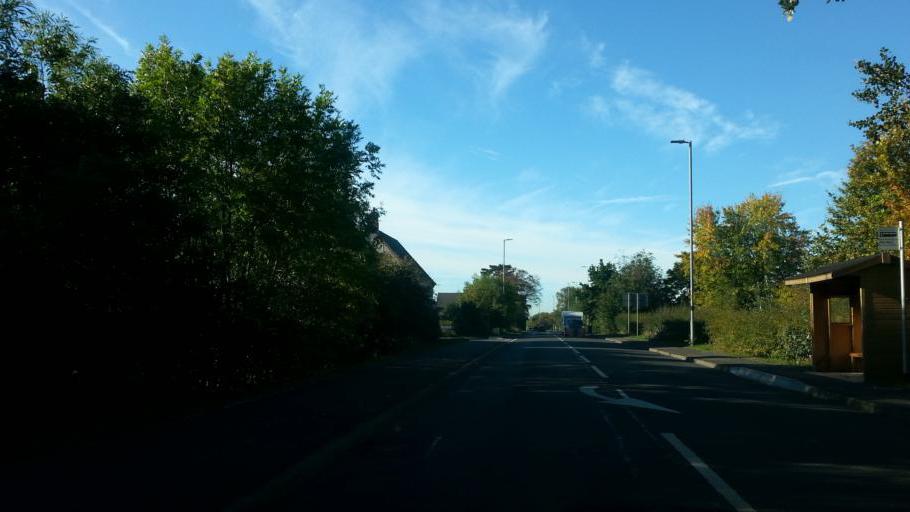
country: GB
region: England
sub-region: Leicestershire
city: Queniborough
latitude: 52.7169
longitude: -1.0452
